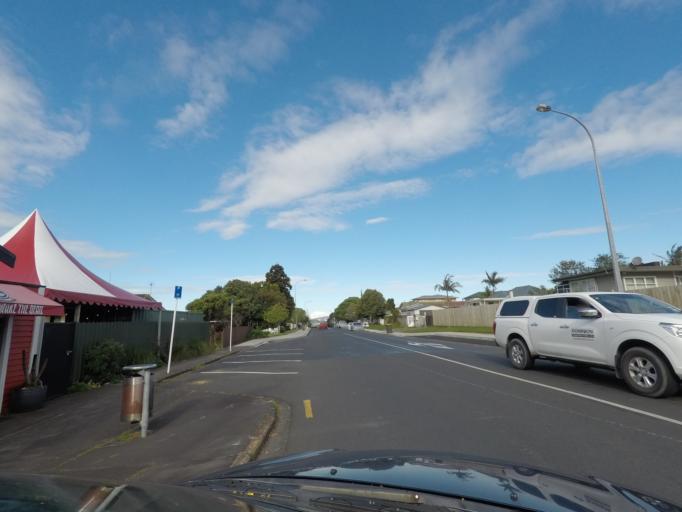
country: NZ
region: Auckland
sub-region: Auckland
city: Rosebank
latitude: -36.8762
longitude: 174.6469
